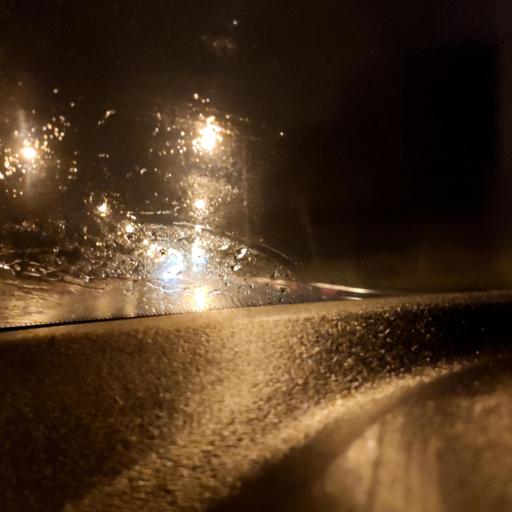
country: RU
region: Samara
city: Volzhskiy
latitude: 53.3592
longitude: 50.2061
